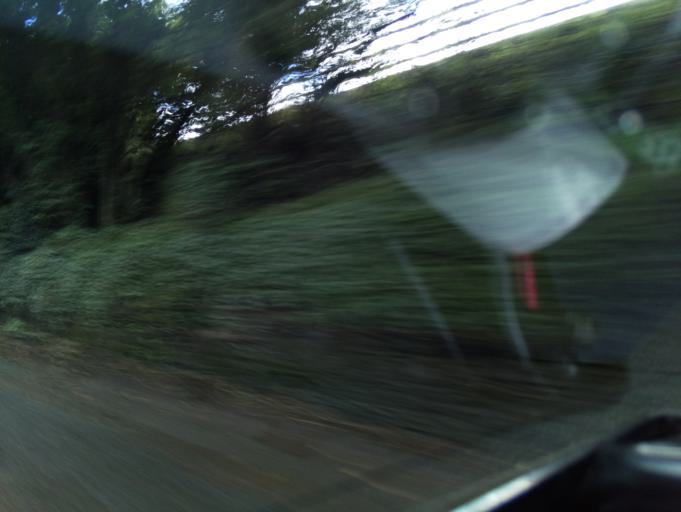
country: GB
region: England
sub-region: Devon
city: Modbury
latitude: 50.3320
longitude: -3.8474
